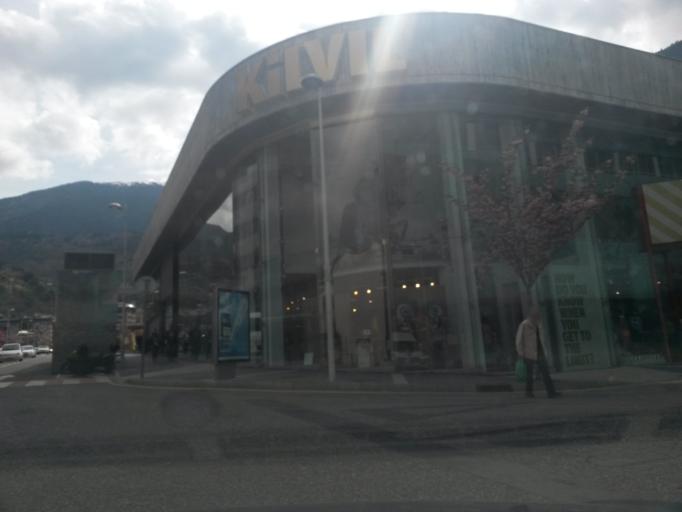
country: AD
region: Escaldes-Engordany
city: les Escaldes
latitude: 42.5093
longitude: 1.5351
